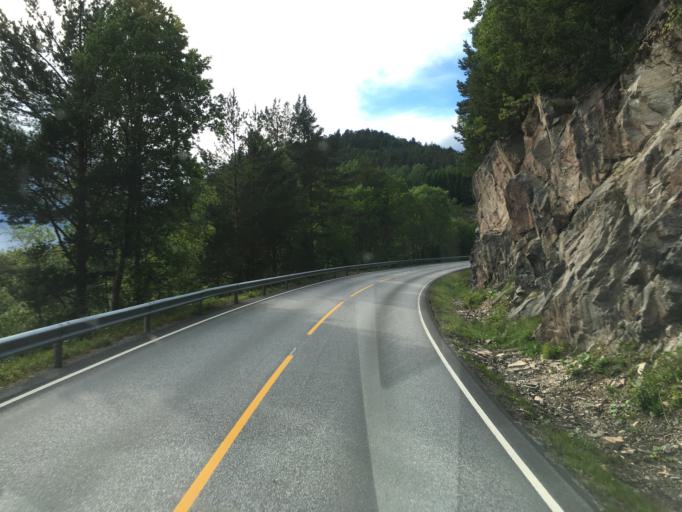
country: NO
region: More og Romsdal
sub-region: Tingvoll
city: Tingvoll
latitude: 62.9743
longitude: 8.0694
